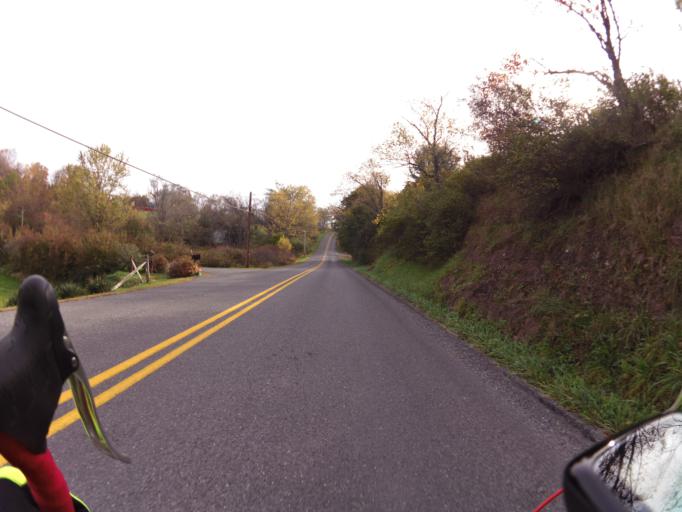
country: US
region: Pennsylvania
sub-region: Union County
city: New Columbia
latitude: 41.0453
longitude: -76.8912
